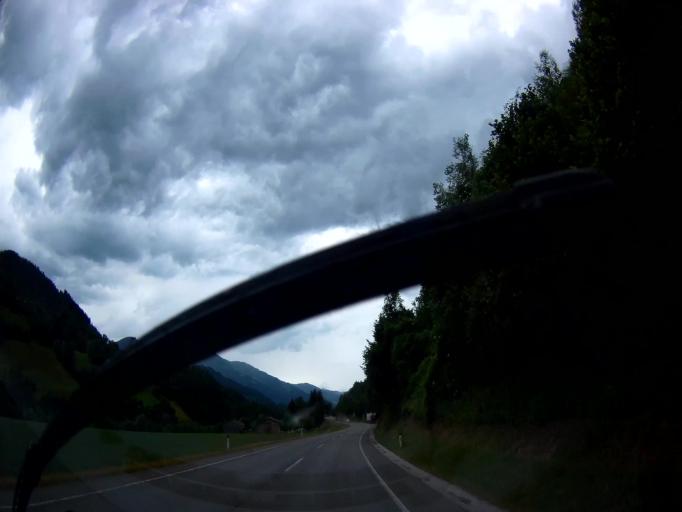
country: AT
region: Salzburg
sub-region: Politischer Bezirk Sankt Johann im Pongau
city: Pfarrwerfen
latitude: 47.4498
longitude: 13.2097
